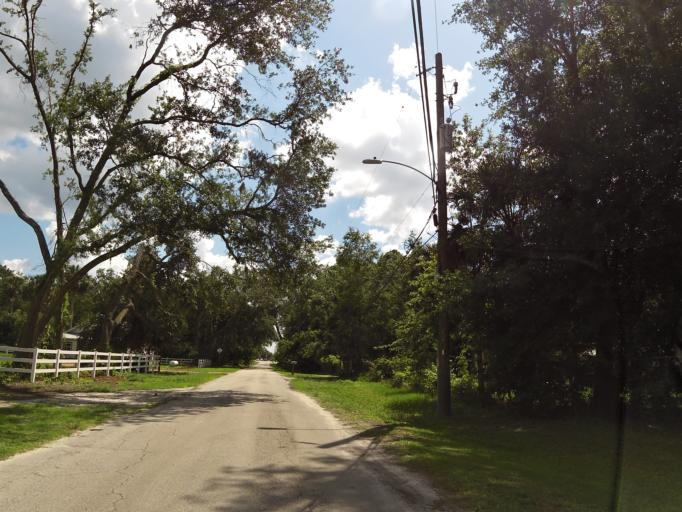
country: US
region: Florida
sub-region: Saint Johns County
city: Palm Valley
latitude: 30.1460
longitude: -81.5148
